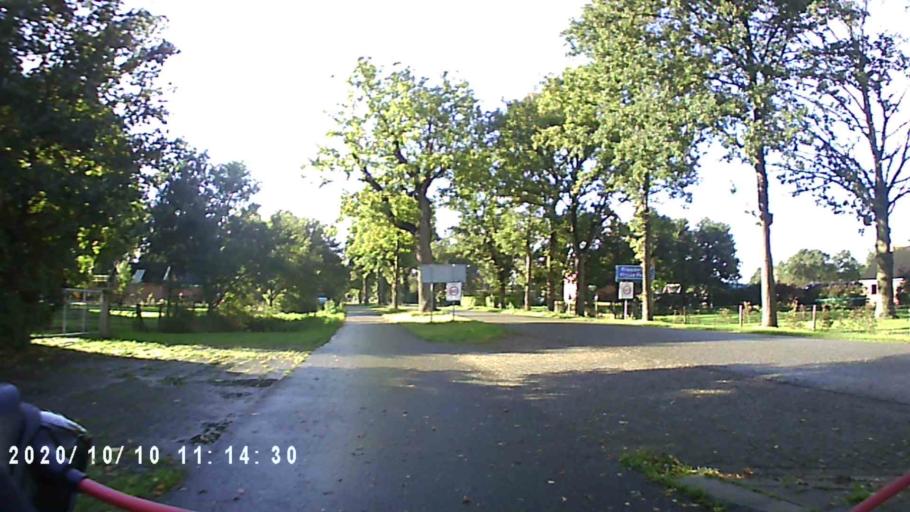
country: NL
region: Friesland
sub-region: Gemeente Smallingerland
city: Drachtstercompagnie
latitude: 53.1056
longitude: 6.2031
